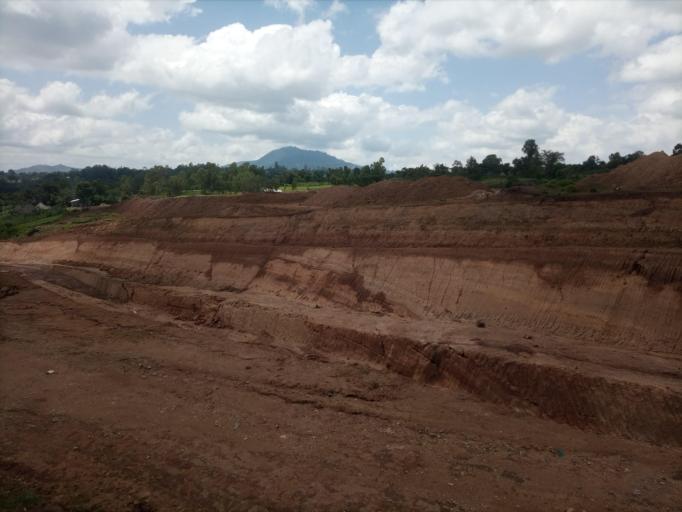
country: ET
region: Southern Nations, Nationalities, and People's Region
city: K'olito
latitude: 7.3070
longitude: 37.9634
